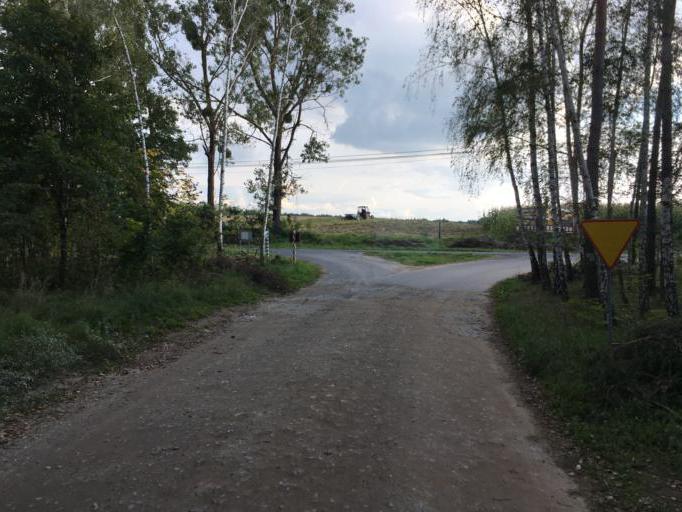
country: PL
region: Kujawsko-Pomorskie
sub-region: Powiat tucholski
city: Tuchola
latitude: 53.6014
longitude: 17.9115
